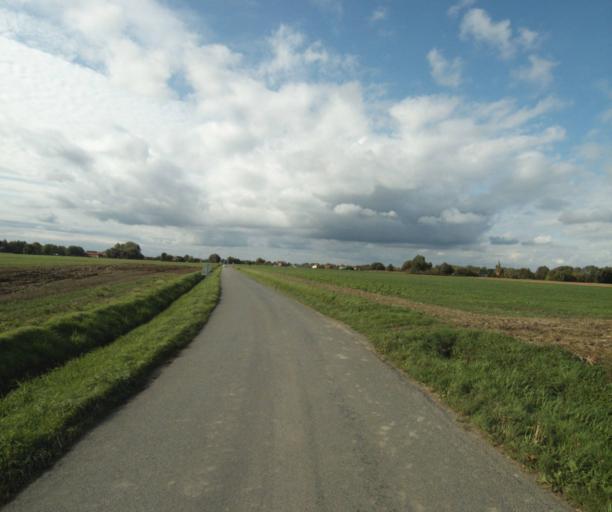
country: FR
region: Nord-Pas-de-Calais
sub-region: Departement du Nord
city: Ennetieres-en-Weppes
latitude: 50.6513
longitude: 2.9277
